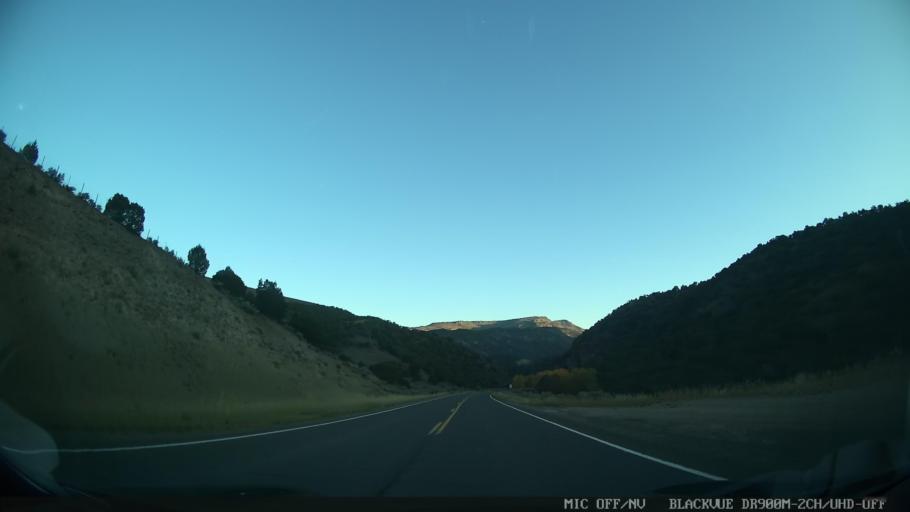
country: US
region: Colorado
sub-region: Eagle County
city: Edwards
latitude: 39.8440
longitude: -106.6428
